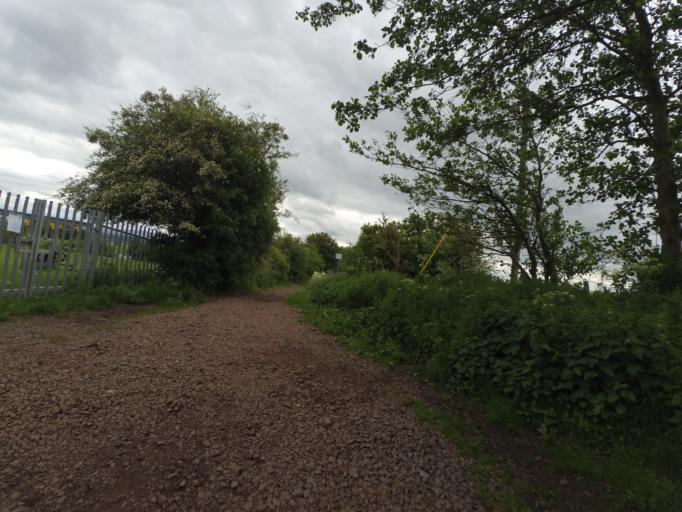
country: GB
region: Scotland
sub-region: East Lothian
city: Tranent
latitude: 55.9208
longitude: -2.9699
